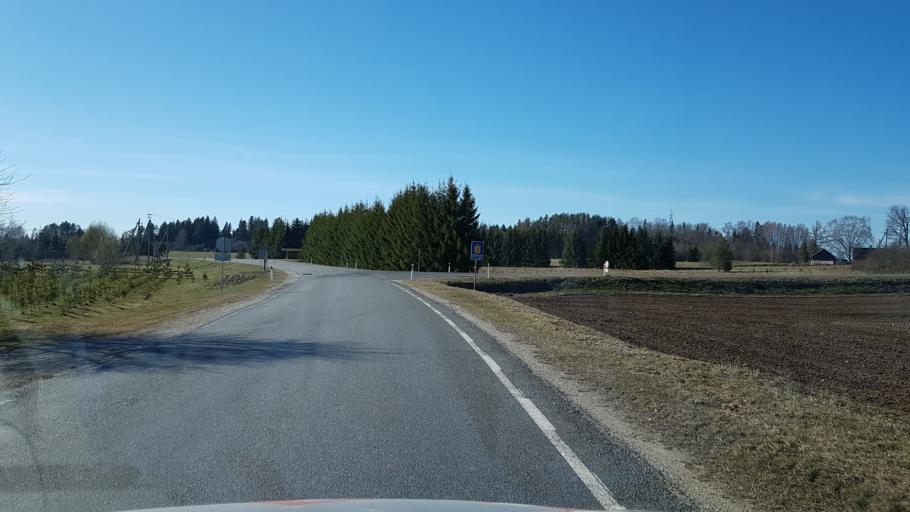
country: EE
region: Laeaene-Virumaa
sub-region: Vinni vald
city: Vinni
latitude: 59.3046
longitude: 26.5673
